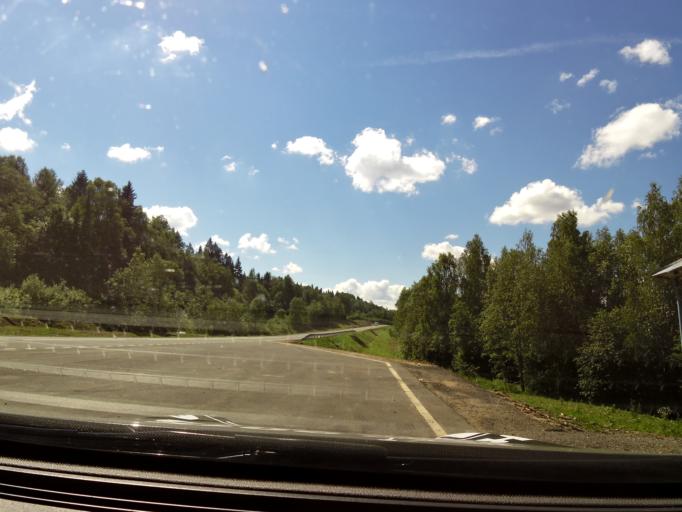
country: RU
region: Vologda
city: Ferapontovo
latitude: 60.0309
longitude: 38.5799
